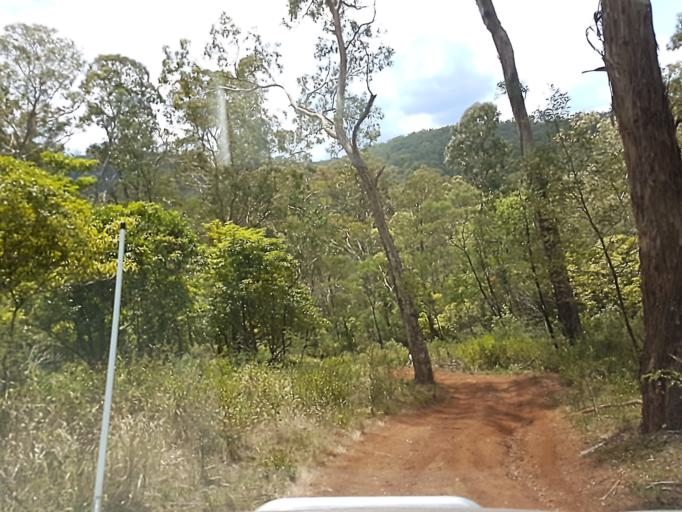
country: AU
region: Victoria
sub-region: East Gippsland
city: Lakes Entrance
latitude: -37.3556
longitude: 148.3571
